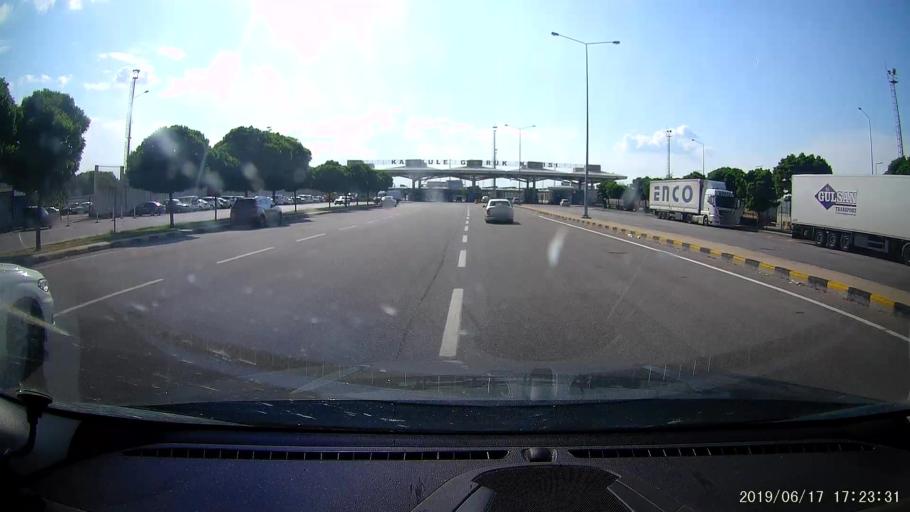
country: GR
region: East Macedonia and Thrace
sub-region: Nomos Evrou
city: Rizia
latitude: 41.7144
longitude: 26.3644
